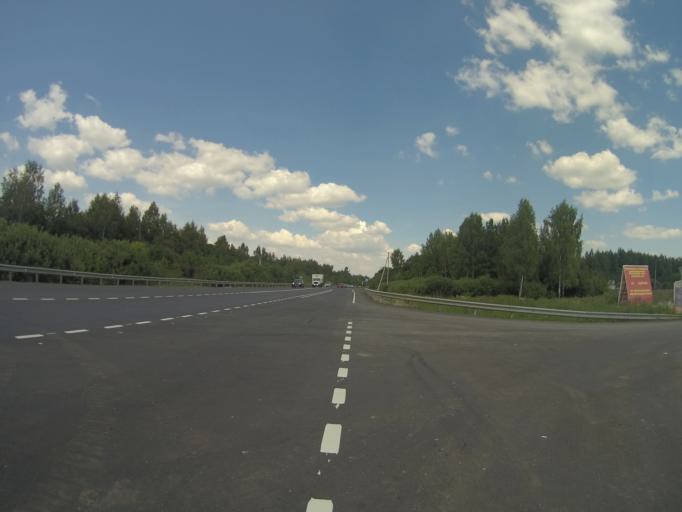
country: RU
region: Kostroma
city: Volgorechensk
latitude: 57.4159
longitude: 41.1952
